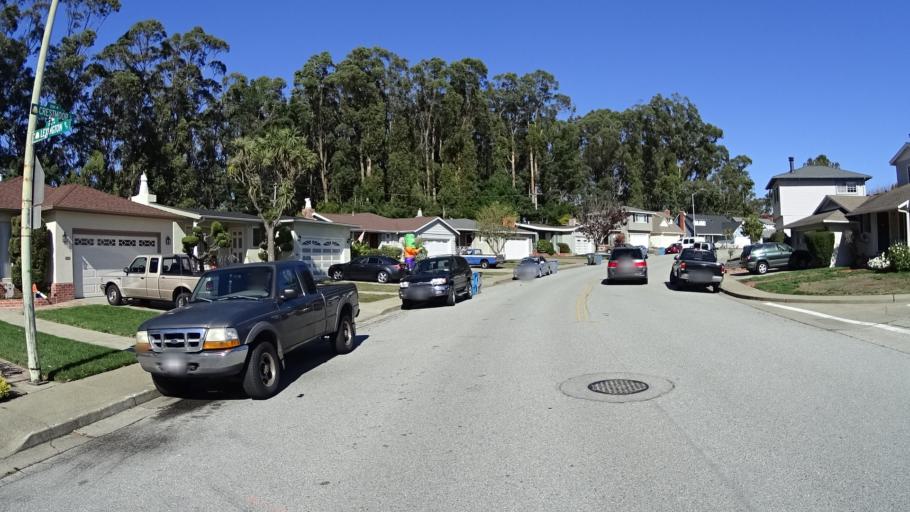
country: US
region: California
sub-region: San Mateo County
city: San Bruno
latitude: 37.6207
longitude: -122.4369
